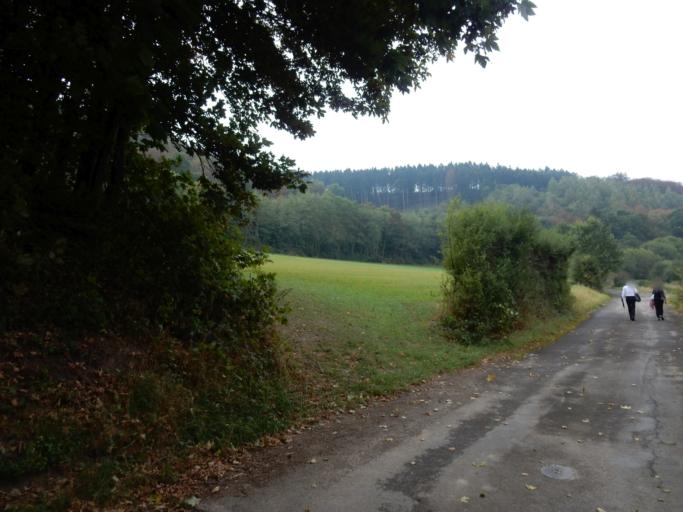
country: LU
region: Diekirch
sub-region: Canton de Wiltz
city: Wiltz
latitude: 49.9618
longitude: 5.9195
